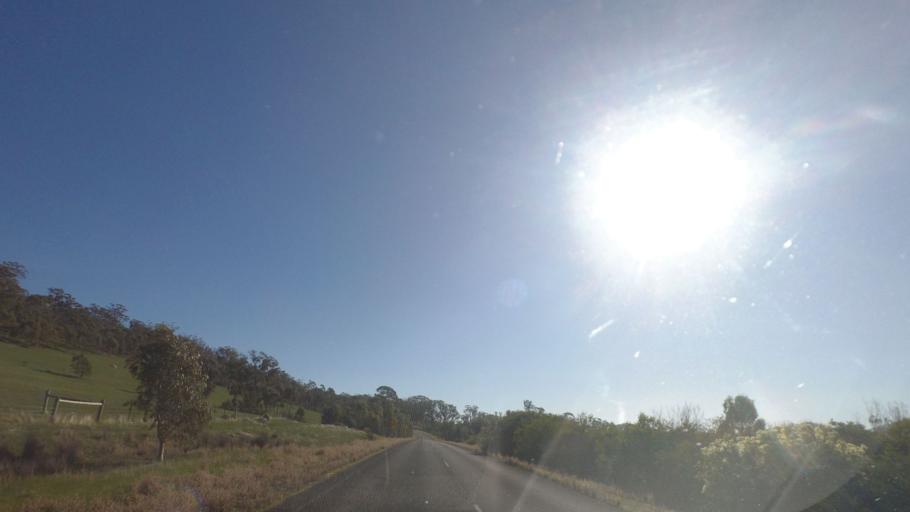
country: AU
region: Victoria
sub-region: Mount Alexander
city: Castlemaine
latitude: -37.0366
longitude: 144.2775
